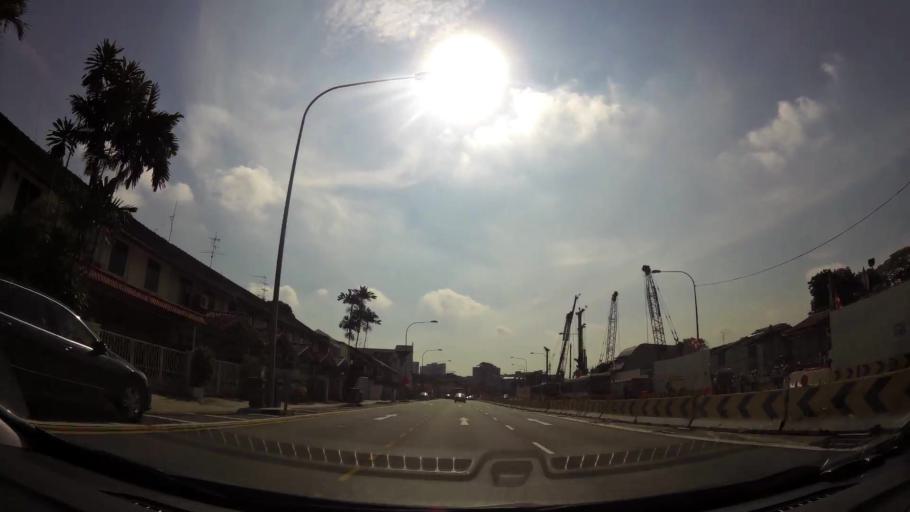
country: SG
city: Singapore
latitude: 1.3550
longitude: 103.8322
